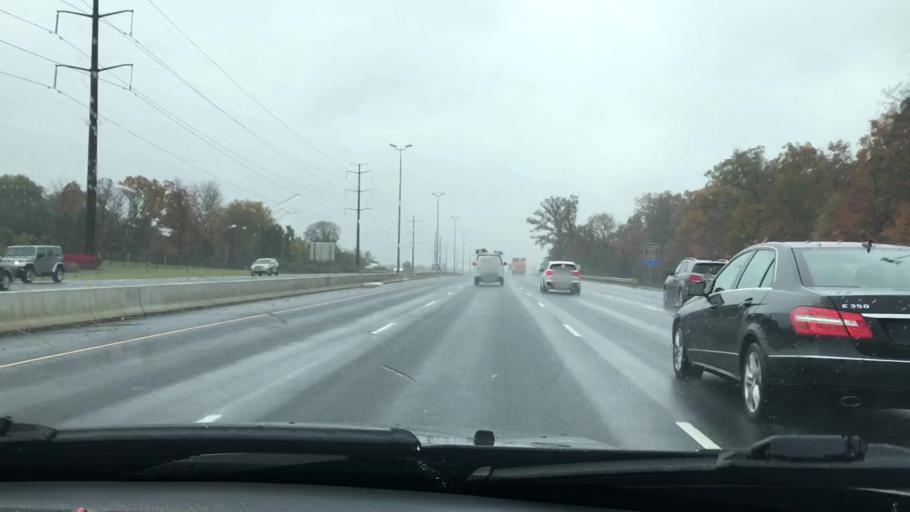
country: US
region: Virginia
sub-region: Fairfax County
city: Floris
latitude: 38.9260
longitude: -77.4302
